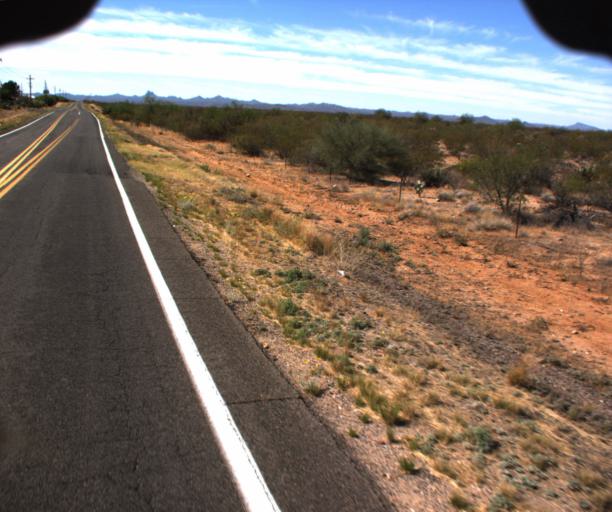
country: US
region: Arizona
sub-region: Yavapai County
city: Congress
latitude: 34.1067
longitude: -112.8321
